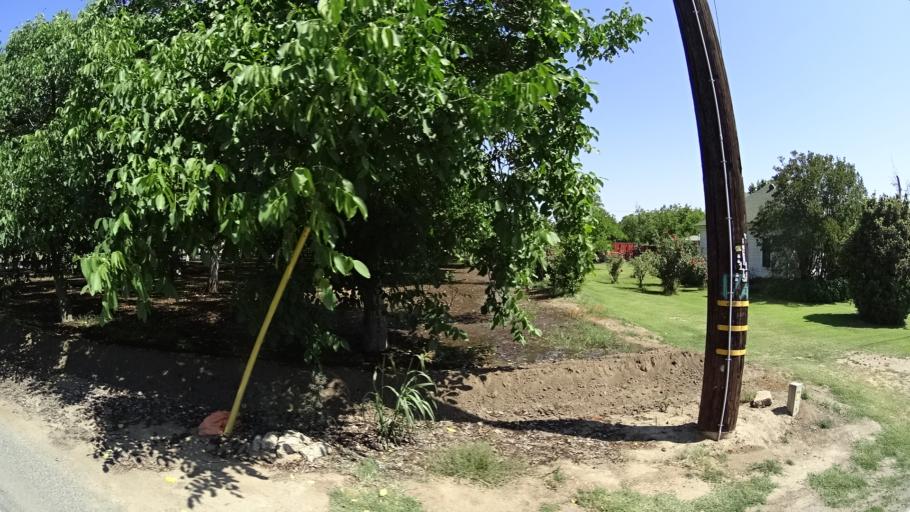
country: US
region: California
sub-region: Kings County
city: Lucerne
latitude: 36.3719
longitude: -119.6541
